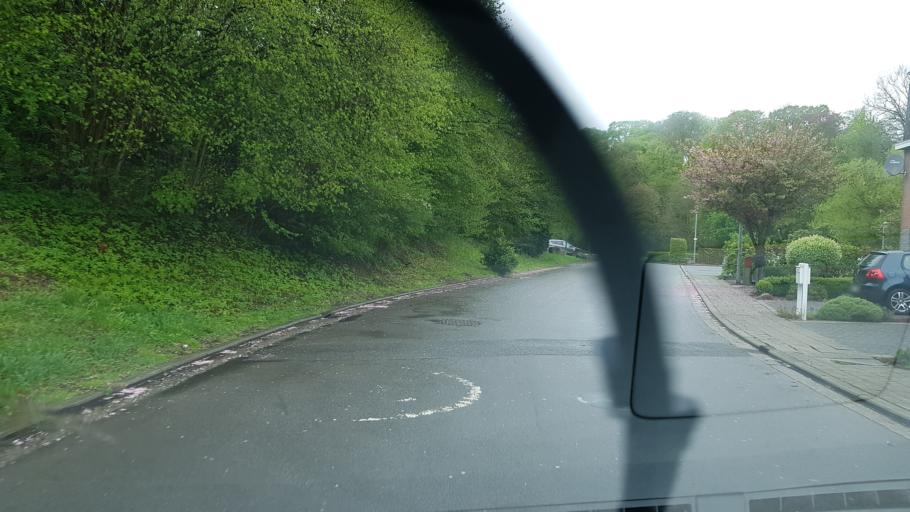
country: BE
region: Wallonia
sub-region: Province de Liege
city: Eupen
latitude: 50.6321
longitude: 6.0458
